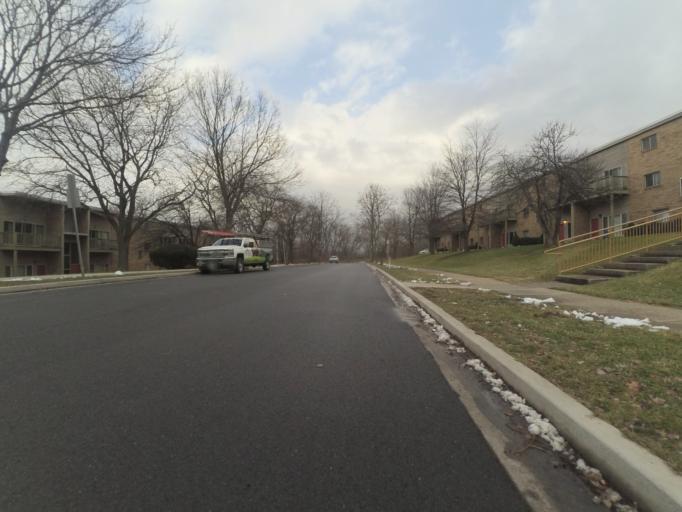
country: US
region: Pennsylvania
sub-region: Centre County
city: State College
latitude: 40.8021
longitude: -77.8444
